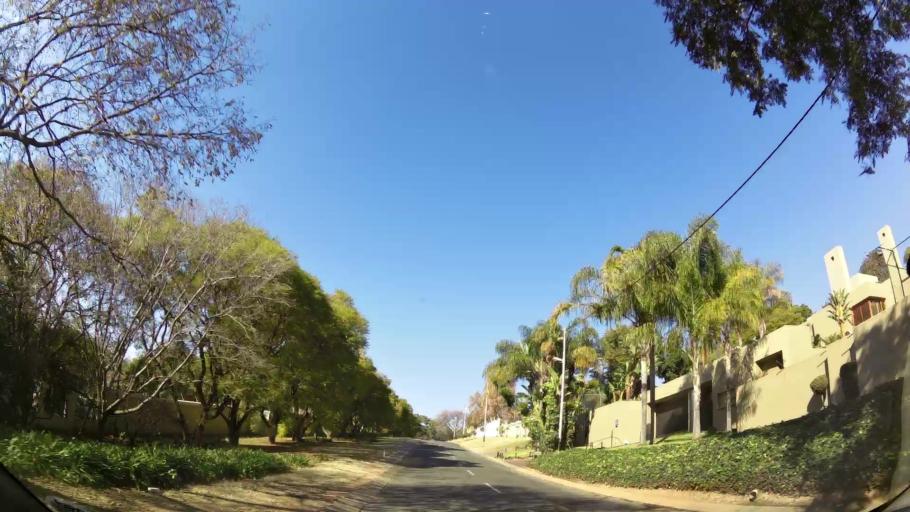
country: ZA
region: Gauteng
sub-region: City of Johannesburg Metropolitan Municipality
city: Midrand
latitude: -26.0505
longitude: 28.0338
